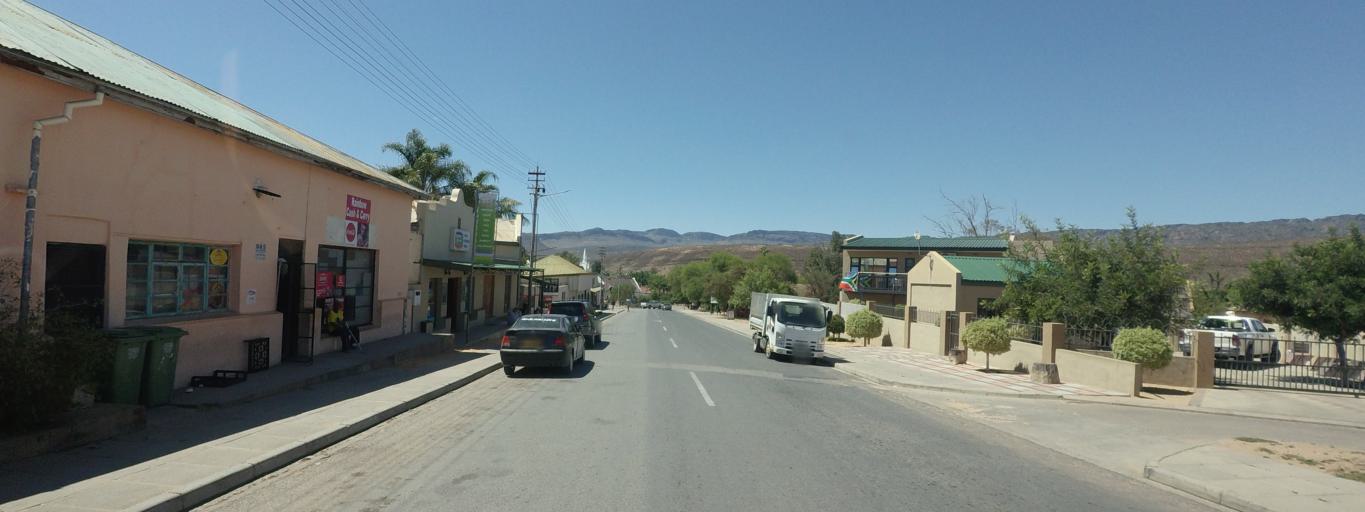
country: ZA
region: Western Cape
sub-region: West Coast District Municipality
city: Clanwilliam
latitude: -32.1824
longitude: 18.8928
